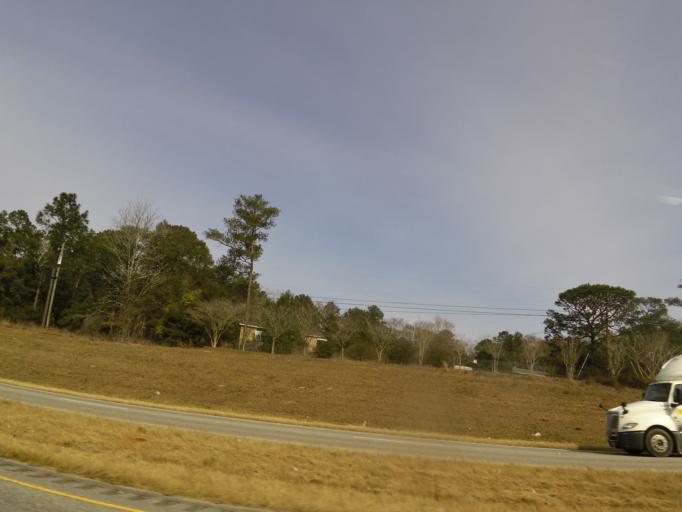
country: US
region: Alabama
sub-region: Dale County
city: Midland City
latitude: 31.2970
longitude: -85.4810
